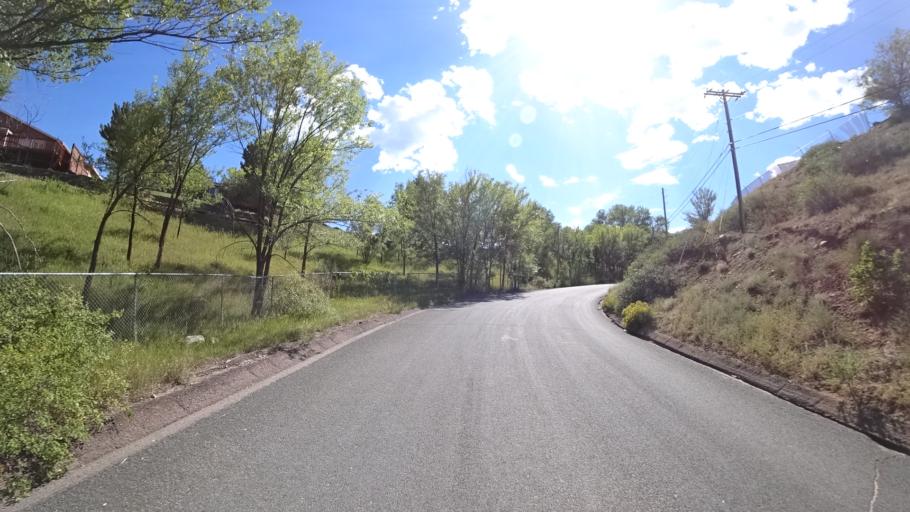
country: US
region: Colorado
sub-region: El Paso County
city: Manitou Springs
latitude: 38.8321
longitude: -104.8753
